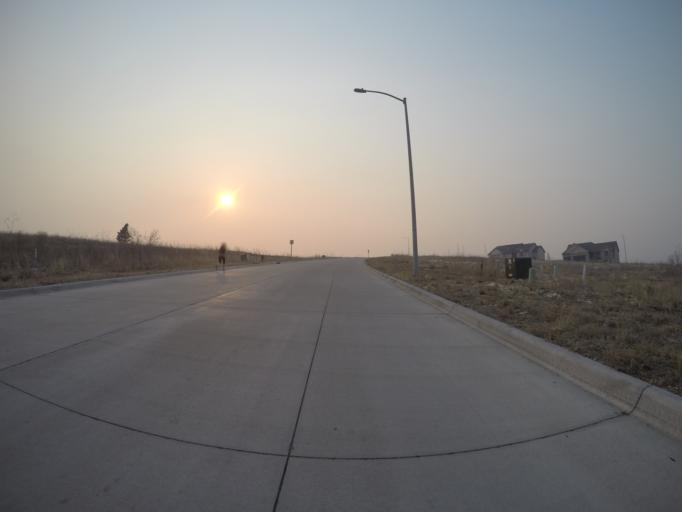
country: US
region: Kansas
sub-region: Riley County
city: Manhattan
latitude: 39.2111
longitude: -96.6370
